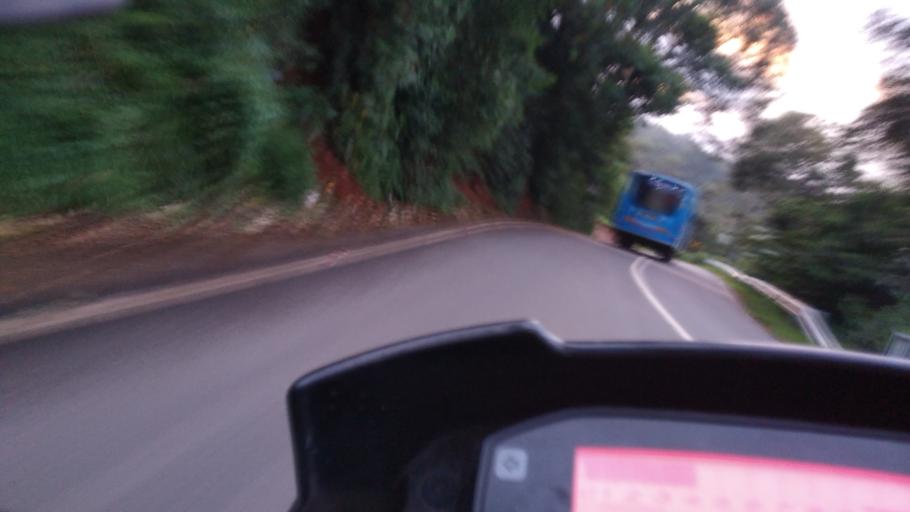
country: IN
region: Kerala
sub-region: Idukki
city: Munnar
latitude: 9.9696
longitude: 77.1246
